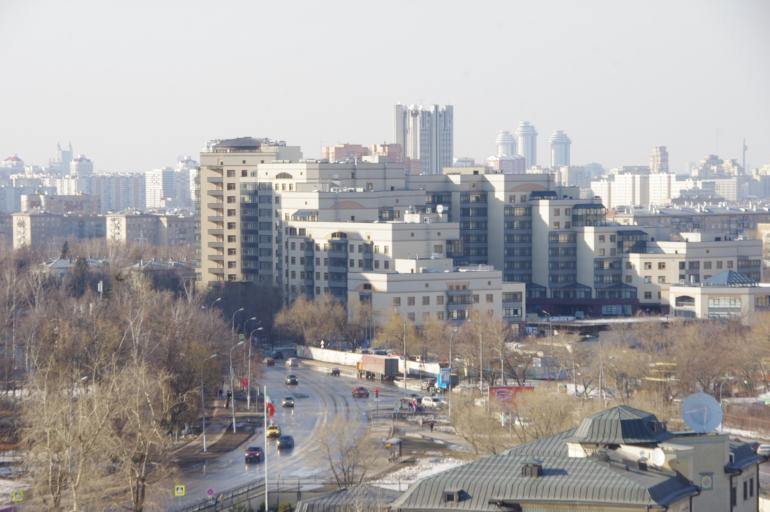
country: RU
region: Moskovskaya
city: Semenovskoye
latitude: 55.6630
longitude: 37.5281
